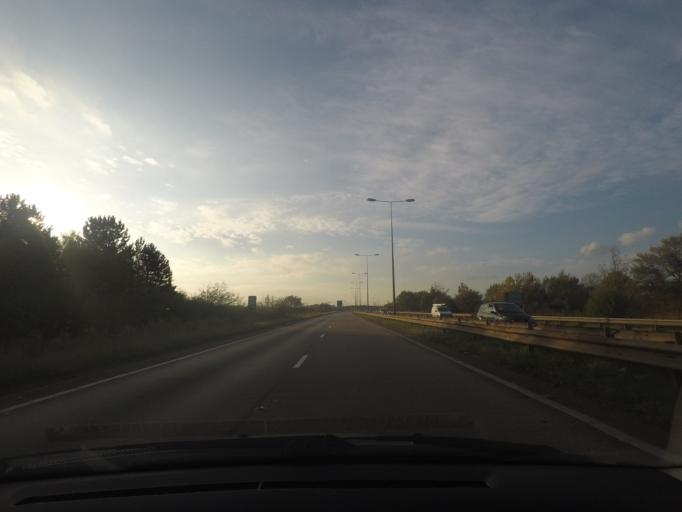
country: GB
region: England
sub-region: North East Lincolnshire
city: Great Coates
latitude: 53.5807
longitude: -0.1252
